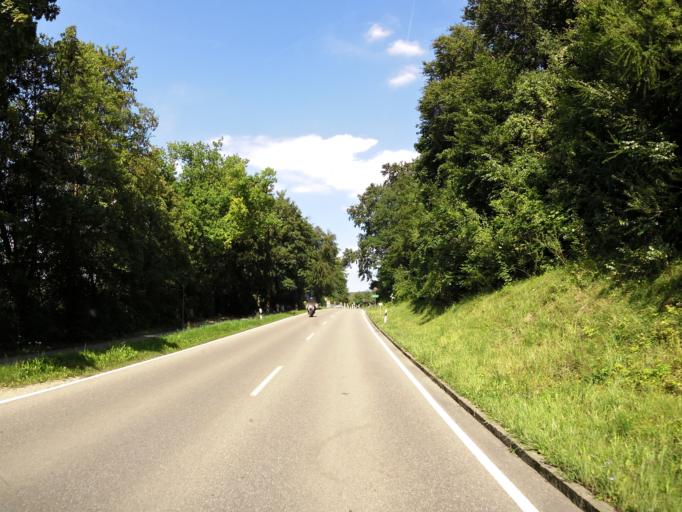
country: DE
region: Bavaria
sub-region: Upper Bavaria
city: Herrsching am Ammersee
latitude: 47.9832
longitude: 11.1613
